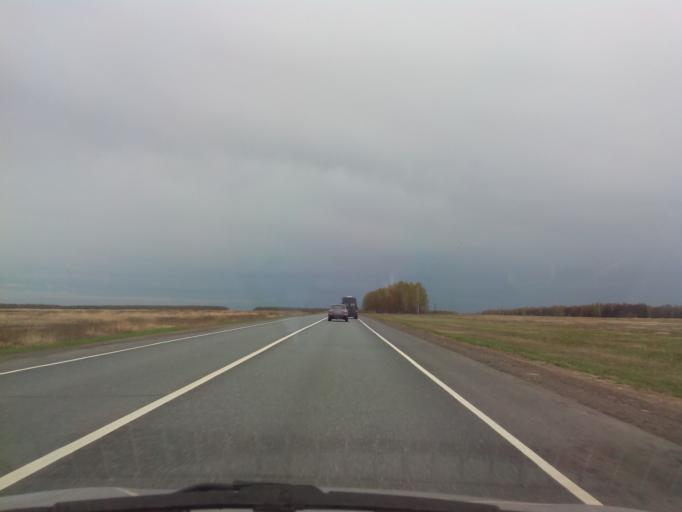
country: RU
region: Moskovskaya
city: Uzunovo
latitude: 54.5305
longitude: 38.4757
